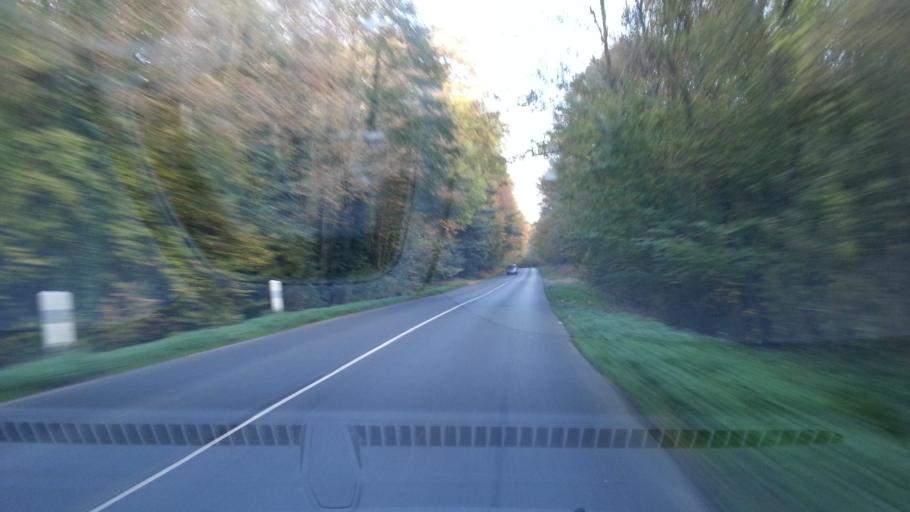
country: FR
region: Picardie
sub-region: Departement de l'Oise
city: Cires-les-Mello
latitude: 49.2677
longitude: 2.3758
